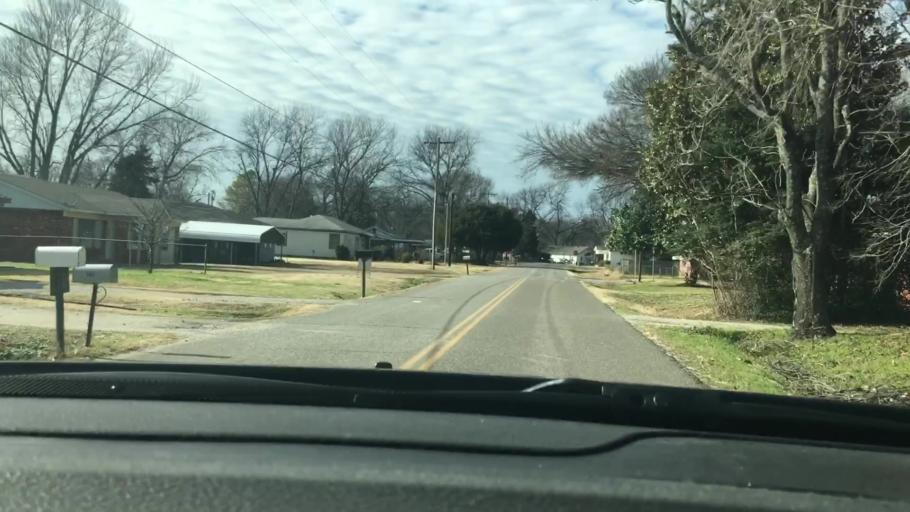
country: US
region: Oklahoma
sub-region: Garvin County
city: Pauls Valley
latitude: 34.7389
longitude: -97.2089
